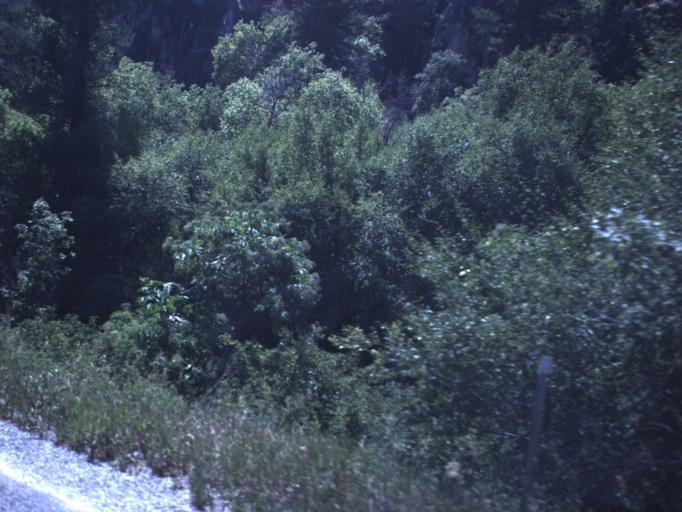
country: US
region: Utah
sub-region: Cache County
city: North Logan
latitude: 41.7944
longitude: -111.6463
